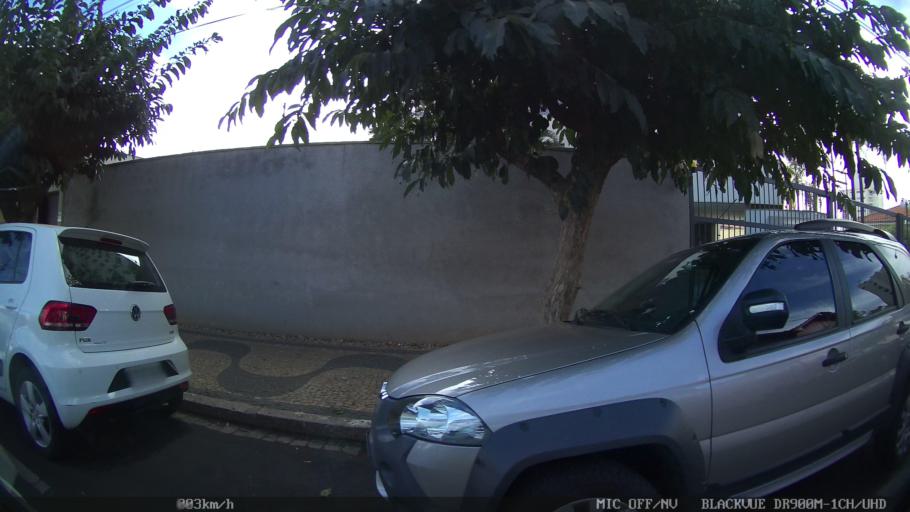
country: BR
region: Sao Paulo
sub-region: Catanduva
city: Catanduva
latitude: -21.1338
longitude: -48.9755
